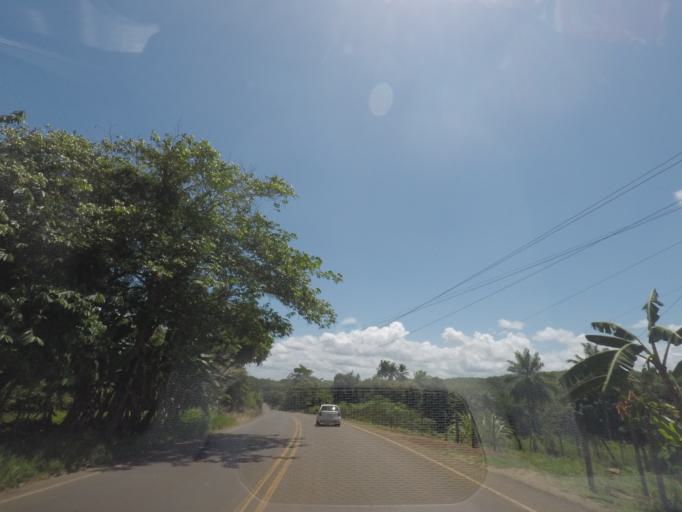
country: BR
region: Bahia
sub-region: Valenca
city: Valenca
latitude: -13.3370
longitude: -39.0639
